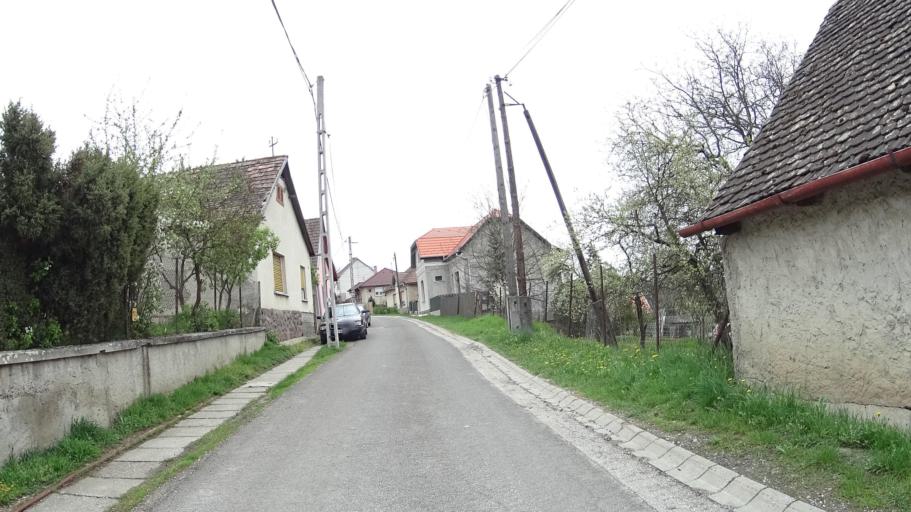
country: HU
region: Pest
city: Kismaros
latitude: 47.8666
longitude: 19.0131
